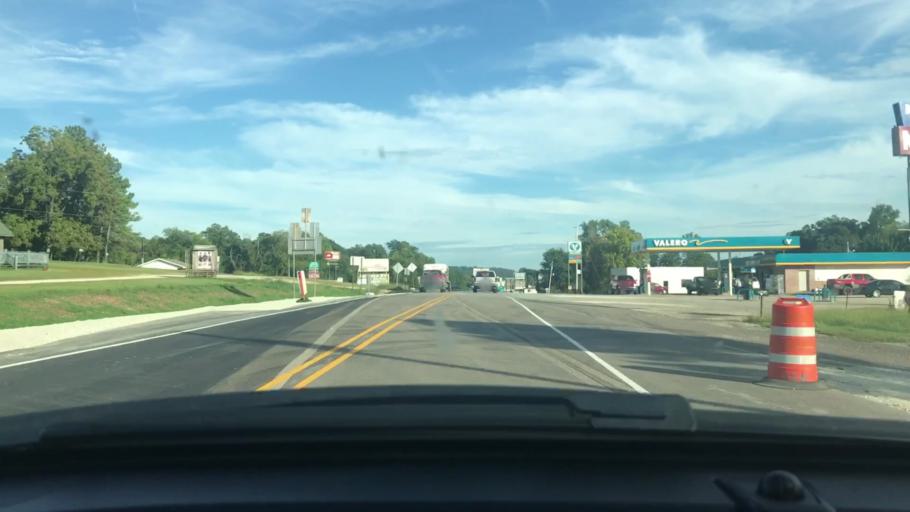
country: US
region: Arkansas
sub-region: Sharp County
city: Cherokee Village
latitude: 36.3029
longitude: -91.4460
